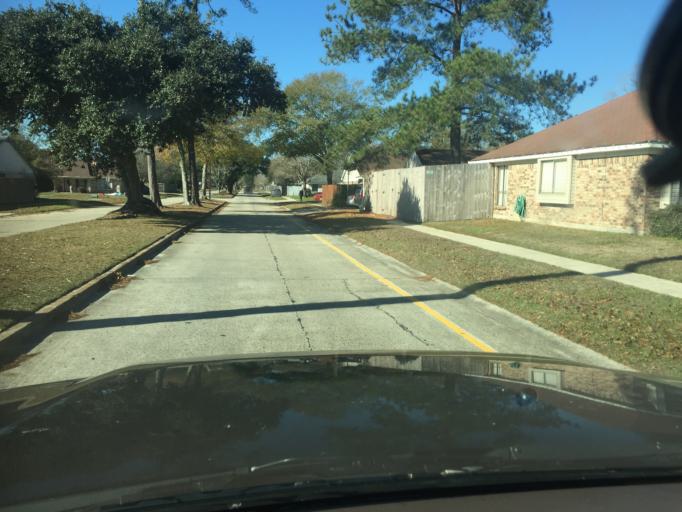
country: US
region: Louisiana
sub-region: Saint Tammany Parish
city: Slidell
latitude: 30.3009
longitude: -89.7301
